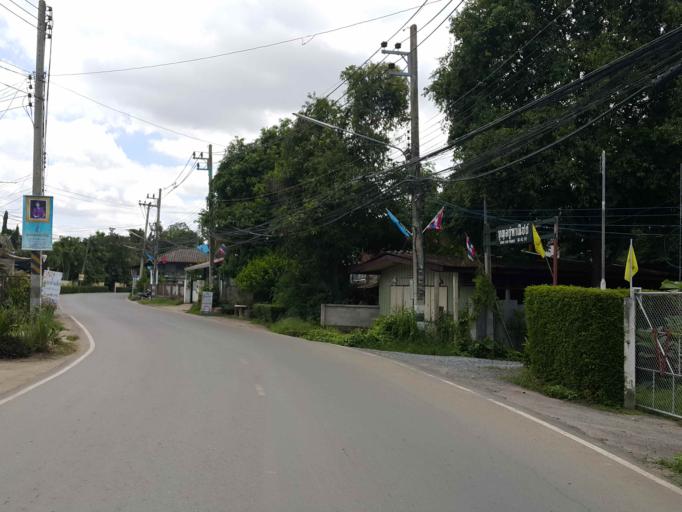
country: TH
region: Chiang Mai
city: Chiang Mai
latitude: 18.8301
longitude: 98.9987
